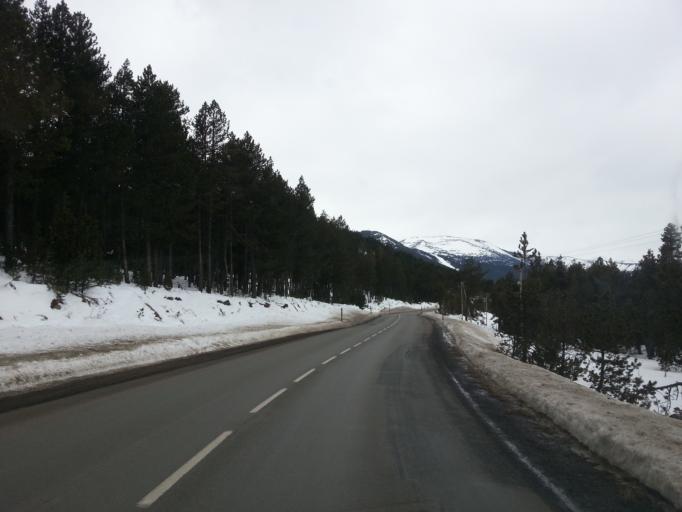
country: ES
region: Catalonia
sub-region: Provincia de Girona
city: Llivia
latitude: 42.5468
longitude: 2.0889
